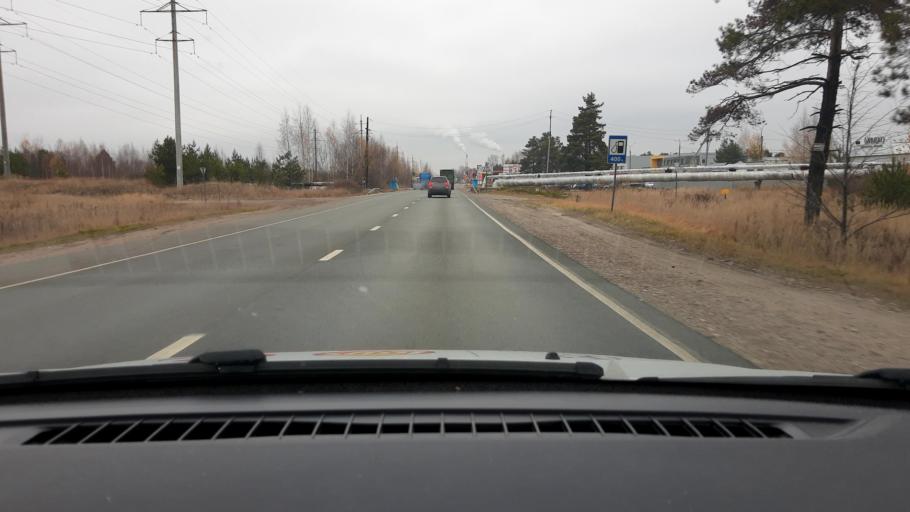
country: RU
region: Nizjnij Novgorod
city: Novaya Balakhna
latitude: 56.4743
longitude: 43.6098
